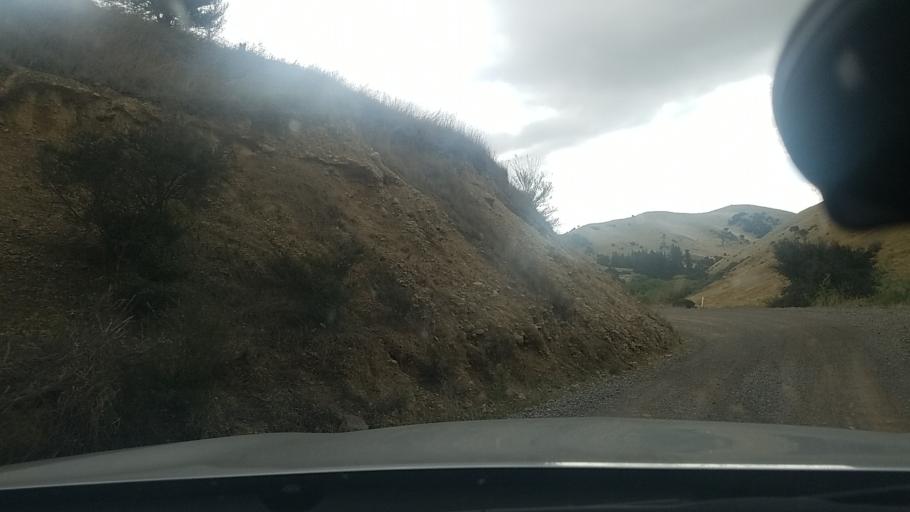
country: NZ
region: Marlborough
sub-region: Marlborough District
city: Blenheim
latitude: -41.5856
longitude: 174.0684
